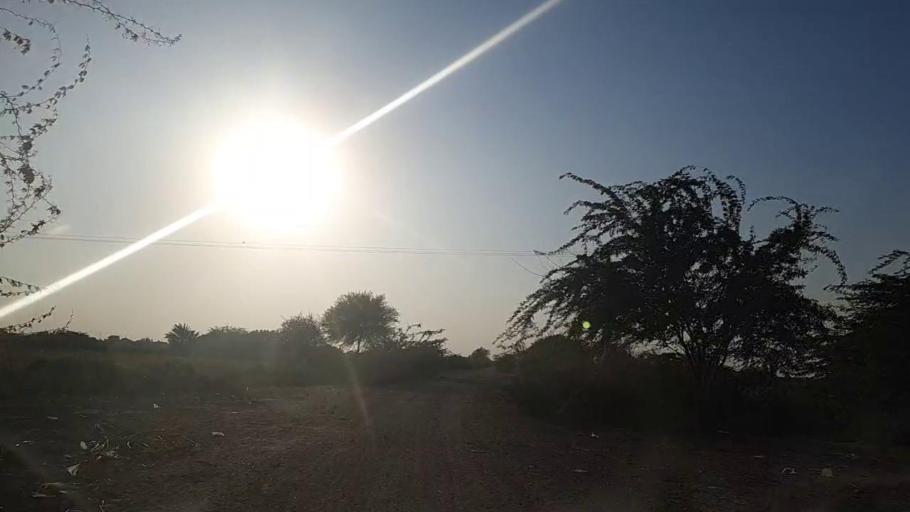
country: PK
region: Sindh
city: Jati
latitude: 24.4169
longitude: 68.1822
